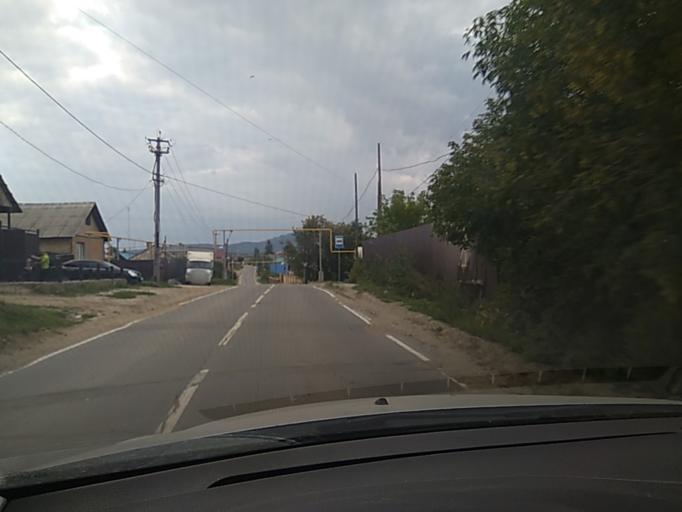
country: RU
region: Chelyabinsk
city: Kyshtym
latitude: 55.6982
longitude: 60.5396
